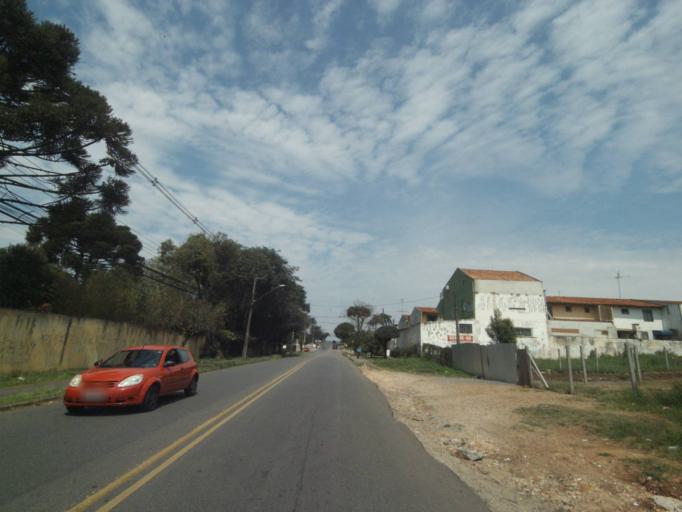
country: BR
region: Parana
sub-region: Pinhais
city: Pinhais
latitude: -25.4241
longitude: -49.2037
